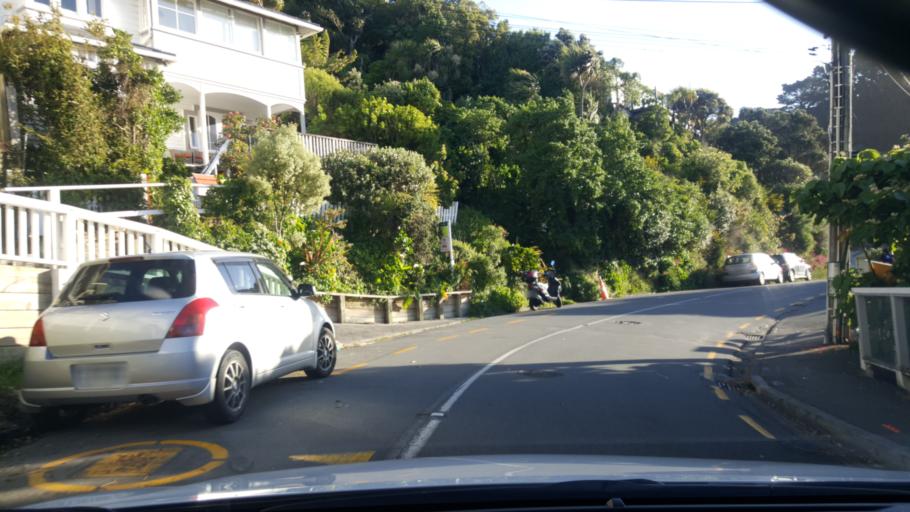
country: NZ
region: Wellington
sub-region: Wellington City
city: Wellington
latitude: -41.2937
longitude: 174.7974
